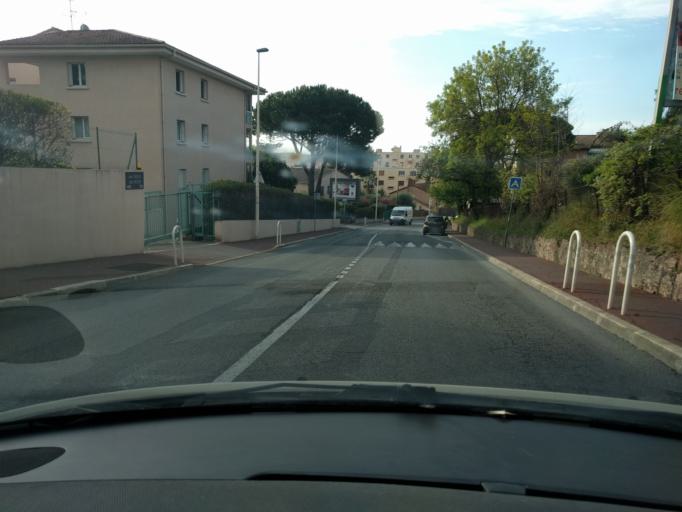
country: FR
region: Provence-Alpes-Cote d'Azur
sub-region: Departement des Alpes-Maritimes
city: Cannes
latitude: 43.5566
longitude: 6.9731
